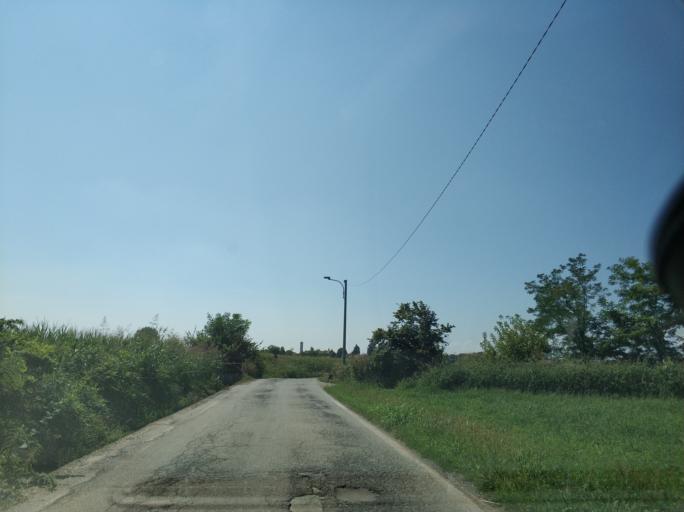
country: IT
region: Piedmont
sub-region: Provincia di Torino
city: San Maurizio
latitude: 45.2251
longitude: 7.6320
